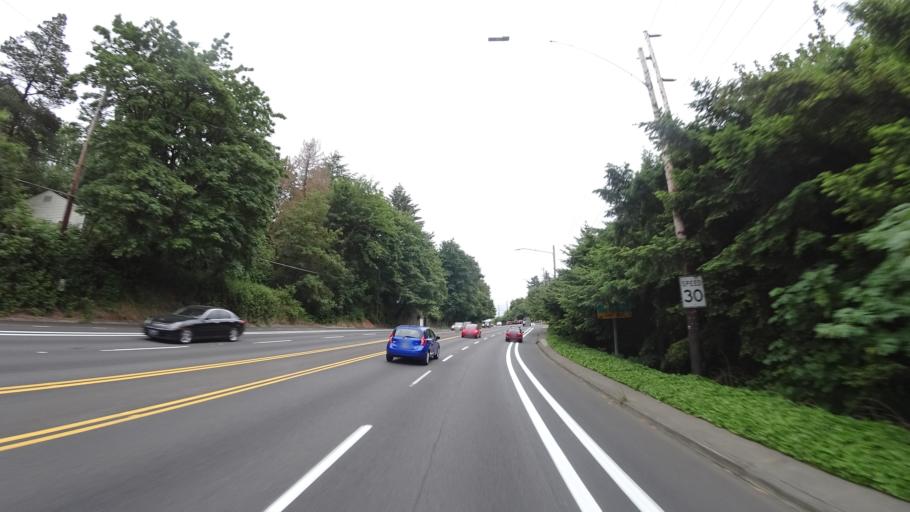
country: US
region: Oregon
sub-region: Multnomah County
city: Portland
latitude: 45.4797
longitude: -122.7016
